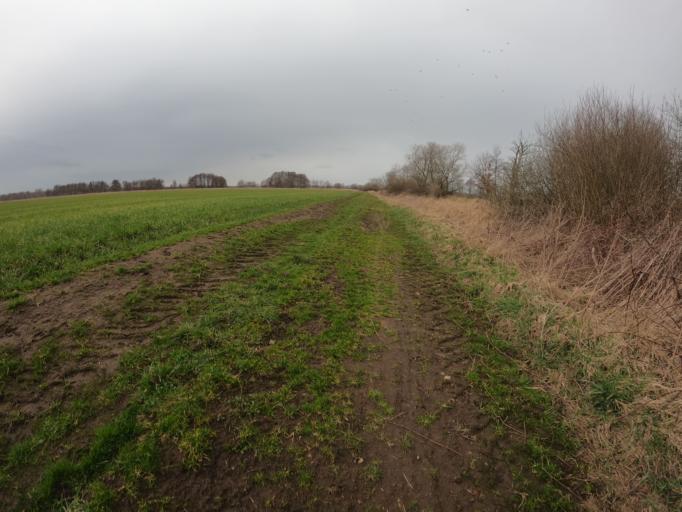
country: PL
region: West Pomeranian Voivodeship
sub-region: Powiat gryficki
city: Trzebiatow
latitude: 54.0747
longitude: 15.2437
